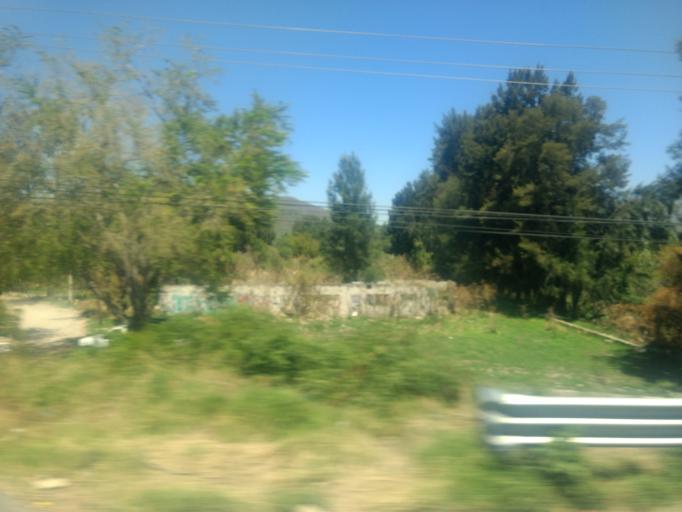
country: MX
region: Jalisco
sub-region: Tlajomulco de Zuniga
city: Santa Cruz de las Flores
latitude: 20.4846
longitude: -103.4949
